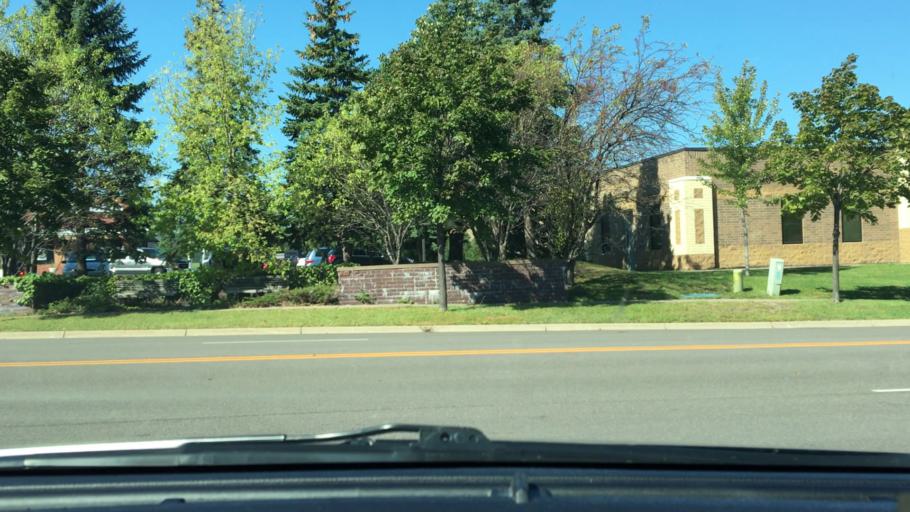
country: US
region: Minnesota
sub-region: Hennepin County
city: Maple Grove
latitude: 45.0673
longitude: -93.4429
